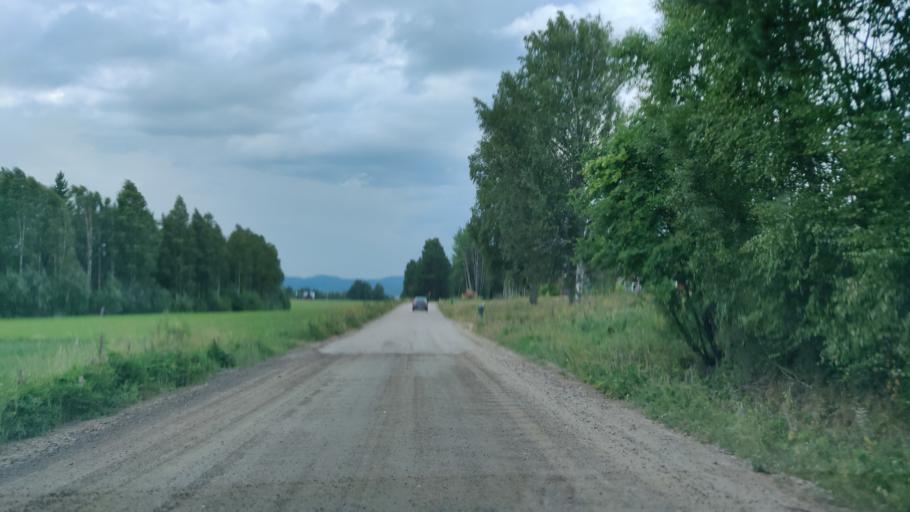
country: SE
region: Vaermland
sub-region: Munkfors Kommun
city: Munkfors
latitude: 59.9635
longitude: 13.4918
